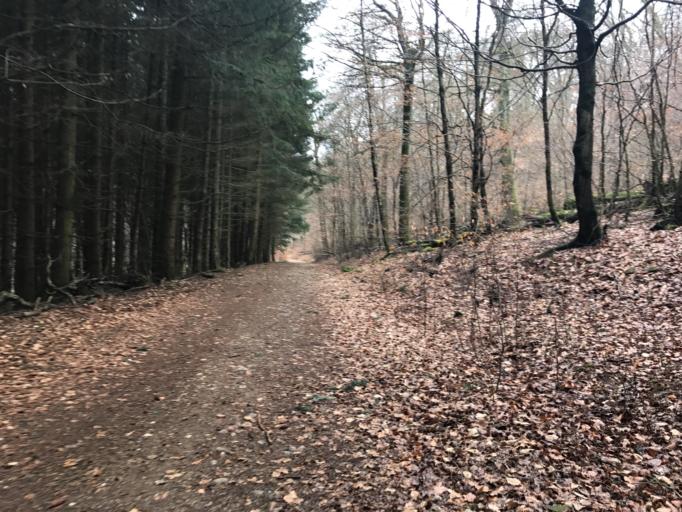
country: DE
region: Hesse
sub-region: Regierungsbezirk Darmstadt
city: Wiesbaden
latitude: 50.1387
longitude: 8.2385
